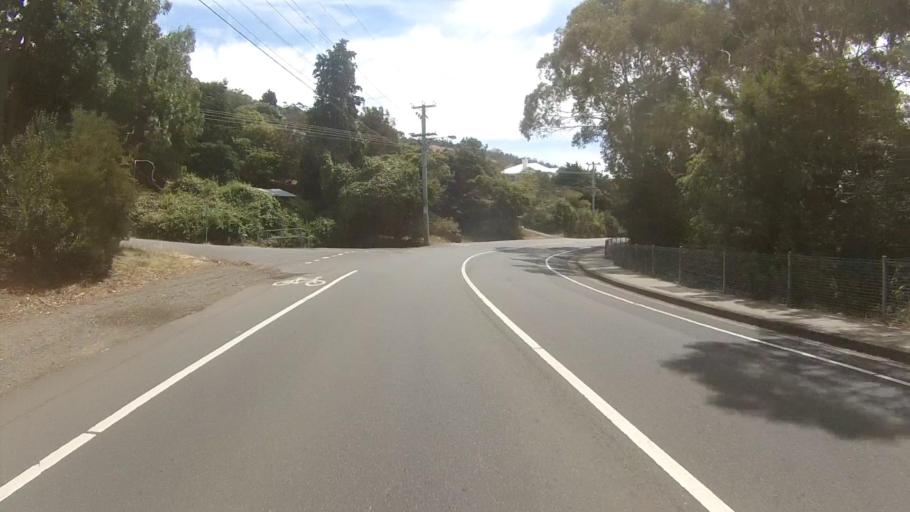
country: AU
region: Tasmania
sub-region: Kingborough
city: Taroona
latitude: -42.9400
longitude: 147.3530
